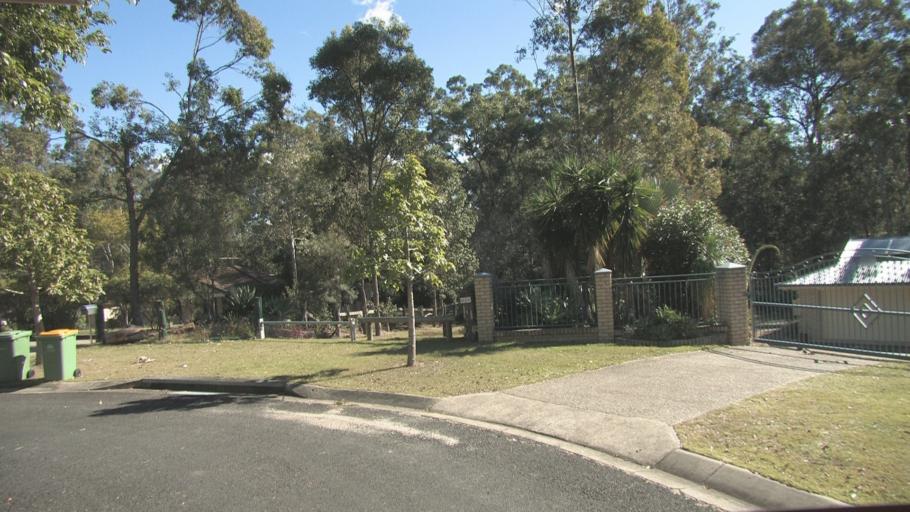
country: AU
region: Queensland
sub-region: Ipswich
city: Springfield Lakes
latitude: -27.7328
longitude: 152.9202
